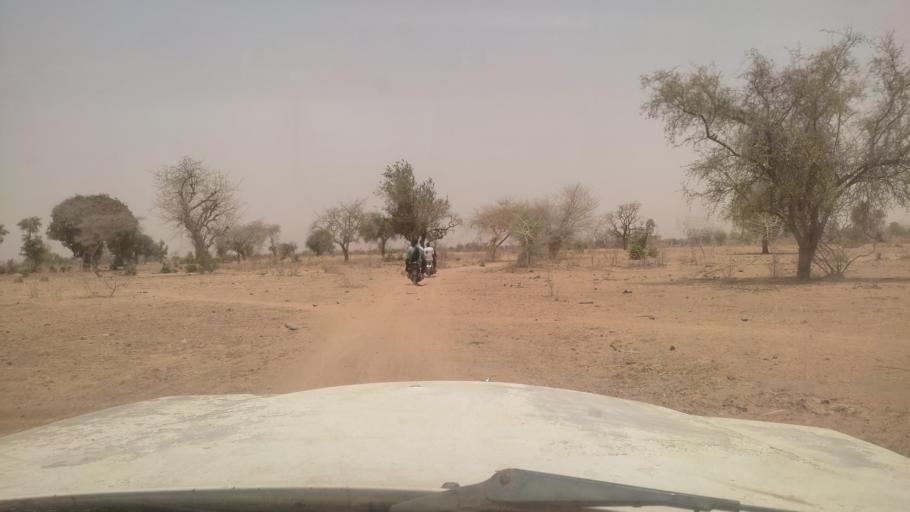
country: BF
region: Est
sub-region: Gnagna Province
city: Bogande
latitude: 13.0323
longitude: -0.0749
